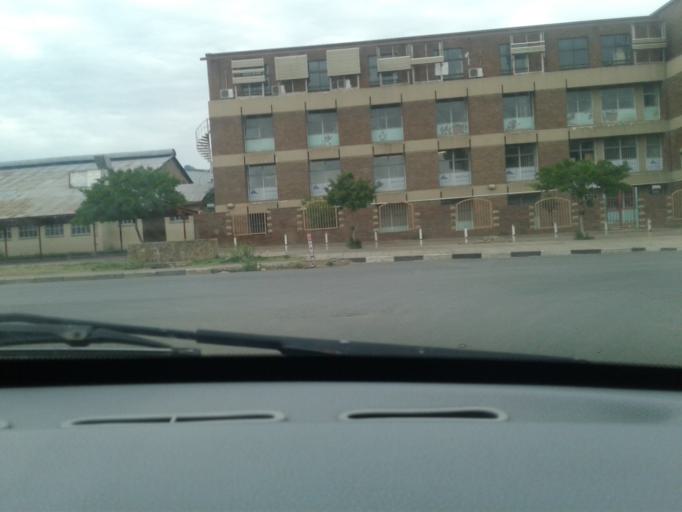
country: LS
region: Maseru
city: Maseru
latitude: -29.2986
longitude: 27.4736
